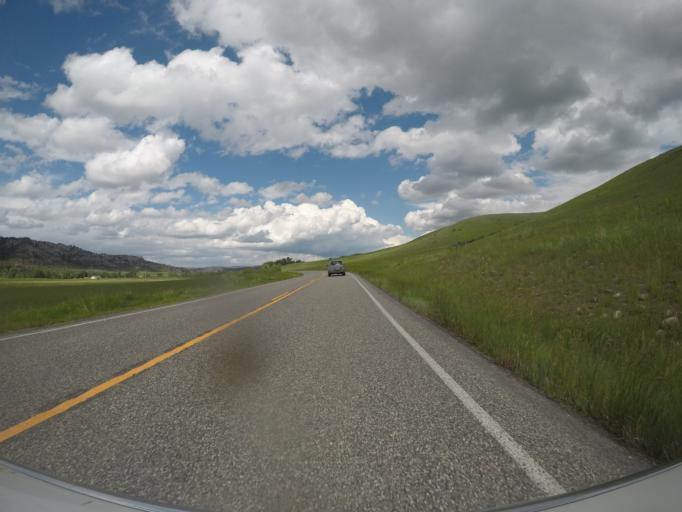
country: US
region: Montana
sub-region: Sweet Grass County
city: Big Timber
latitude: 45.6919
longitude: -110.0411
